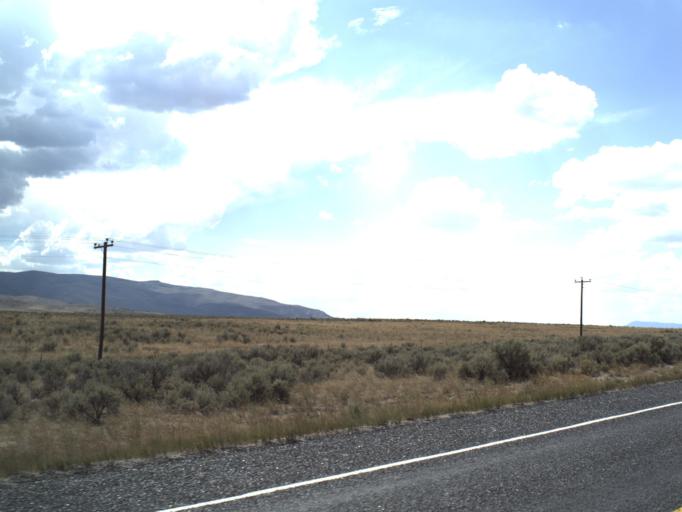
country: US
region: Idaho
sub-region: Minidoka County
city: Rupert
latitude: 41.9875
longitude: -113.1788
